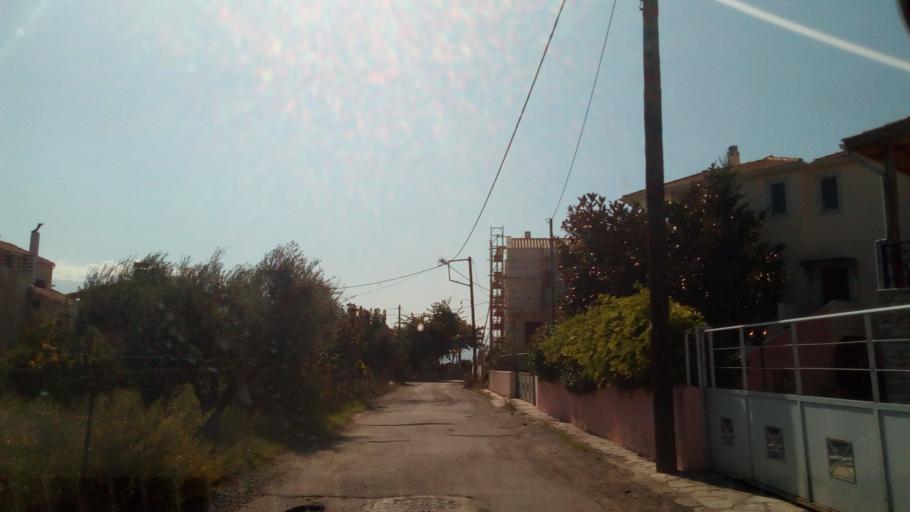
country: GR
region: West Greece
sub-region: Nomos Aitolias kai Akarnanias
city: Nafpaktos
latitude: 38.3754
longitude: 21.7944
